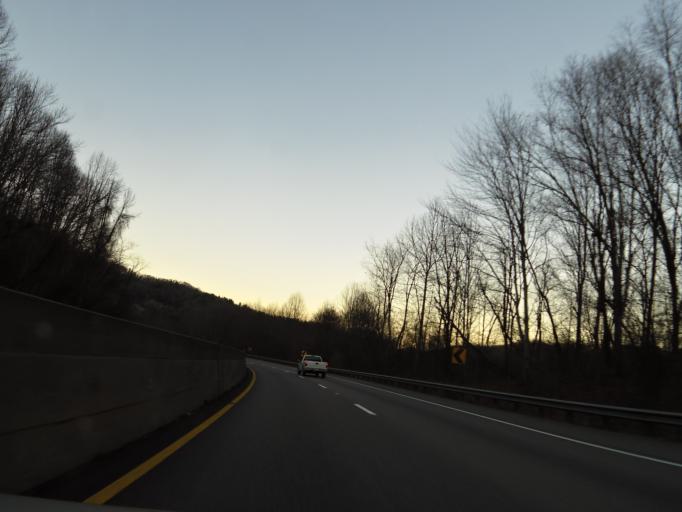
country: US
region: North Carolina
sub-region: Haywood County
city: Cove Creek
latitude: 35.6203
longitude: -83.0082
